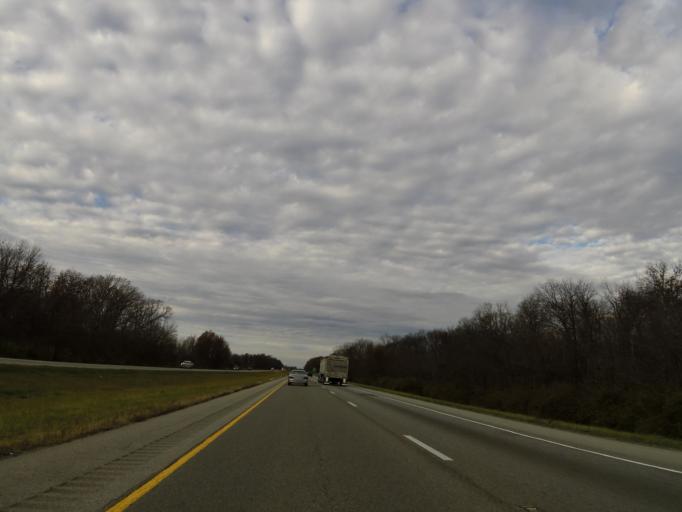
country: US
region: Illinois
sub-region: Clinton County
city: Wamac
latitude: 38.3874
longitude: -89.1415
